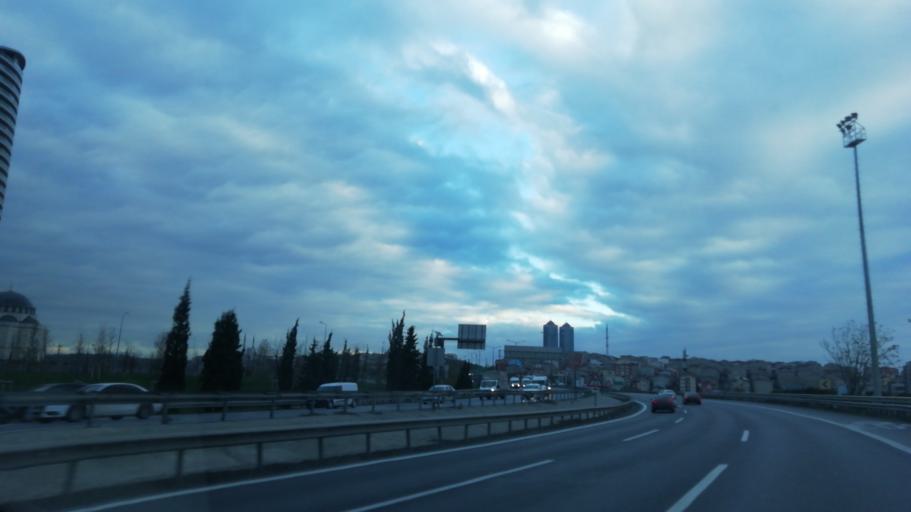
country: TR
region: Istanbul
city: Mahmutbey
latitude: 41.0612
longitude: 28.8443
